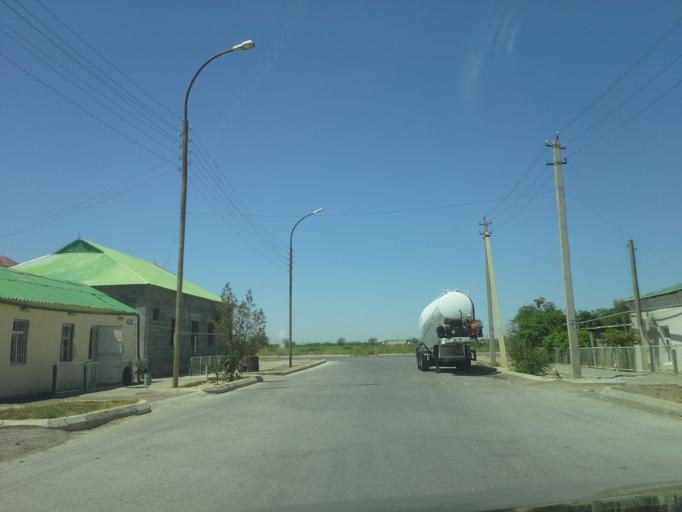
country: TM
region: Ahal
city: Abadan
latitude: 38.0260
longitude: 58.2545
